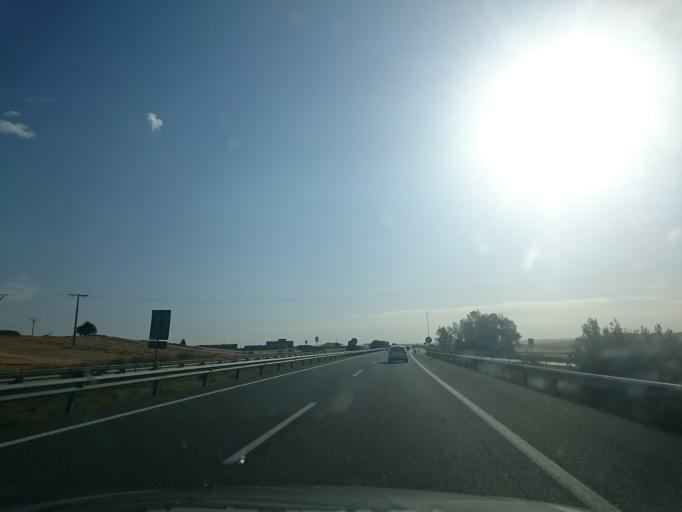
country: ES
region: Castille and Leon
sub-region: Provincia de Burgos
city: Villagonzalo-Pedernales
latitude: 42.3090
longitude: -3.7233
